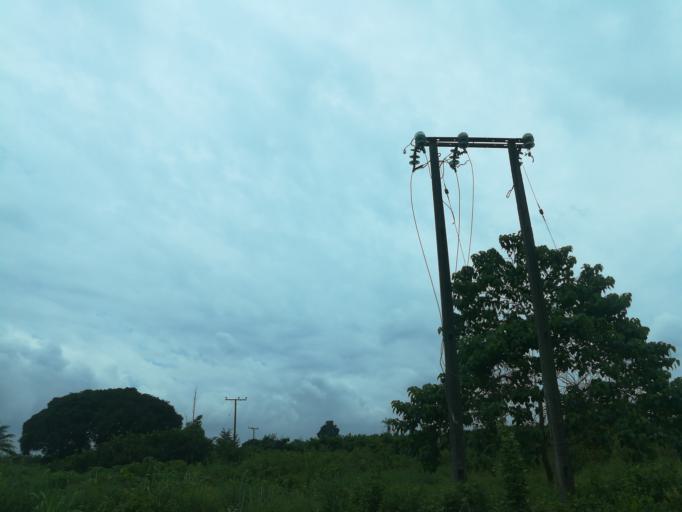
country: NG
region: Lagos
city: Ejirin
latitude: 6.6590
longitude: 3.8177
